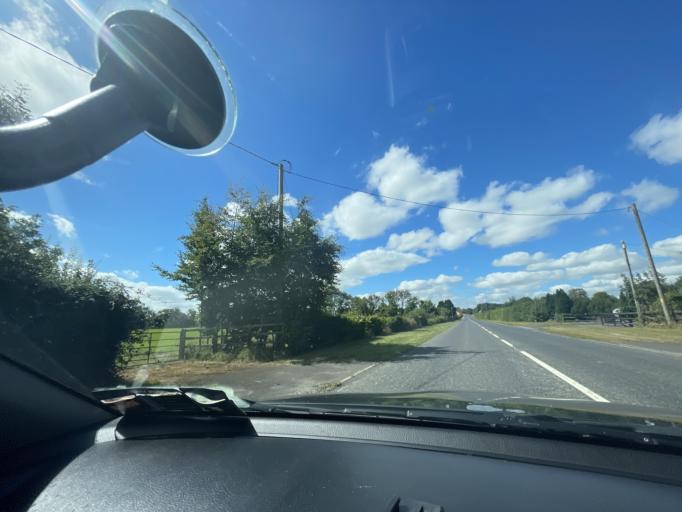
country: IE
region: Leinster
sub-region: An Mhi
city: Newtown Trim
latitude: 53.5289
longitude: -6.6820
